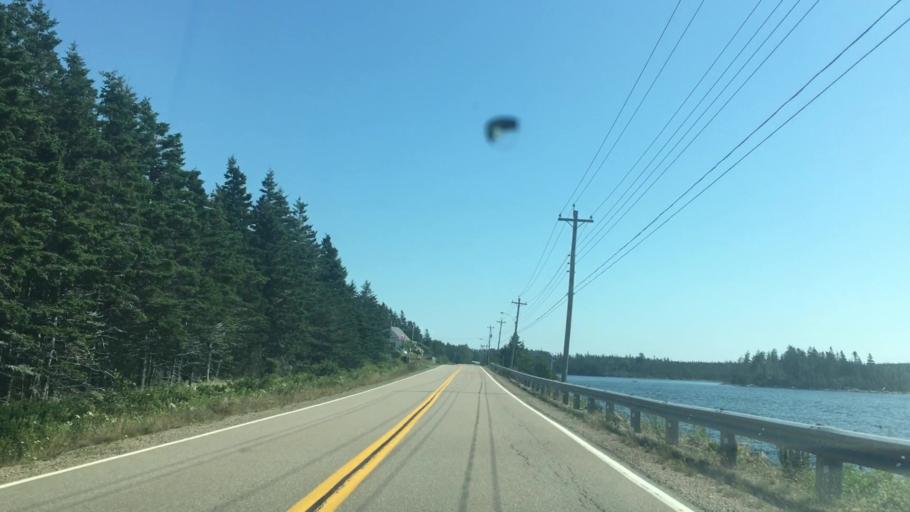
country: CA
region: Nova Scotia
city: Antigonish
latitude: 45.0228
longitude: -62.0179
